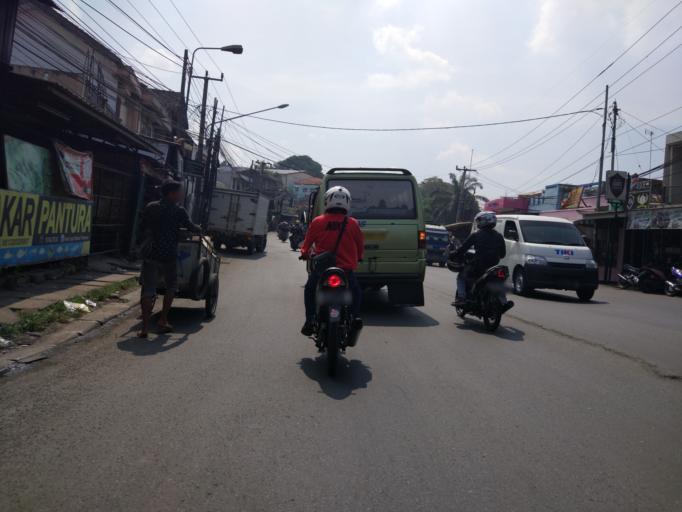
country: ID
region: West Java
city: Cileunyi
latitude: -6.9397
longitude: 107.7521
